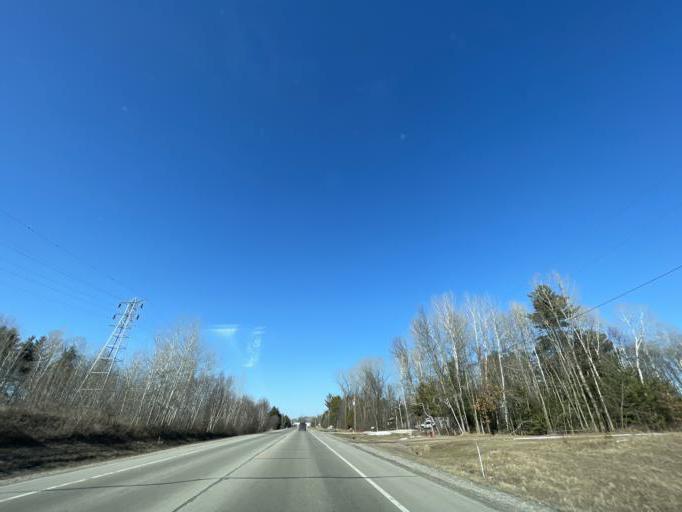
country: US
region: Wisconsin
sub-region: Brown County
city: Suamico
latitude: 44.5966
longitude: -88.0779
